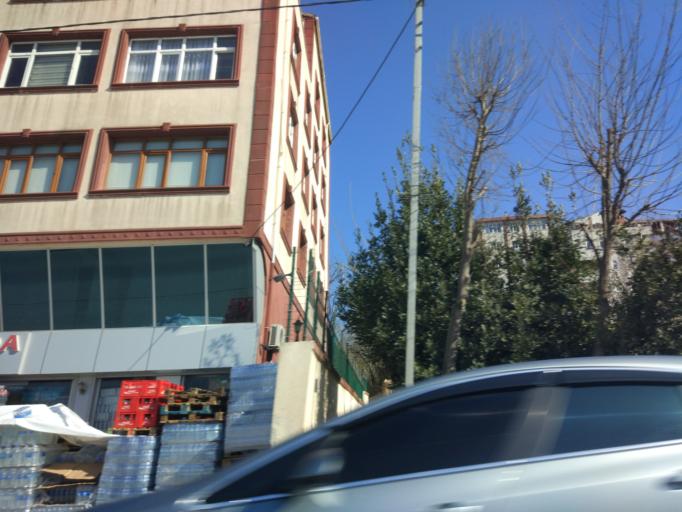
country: TR
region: Istanbul
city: Basaksehir
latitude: 41.0521
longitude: 28.7497
